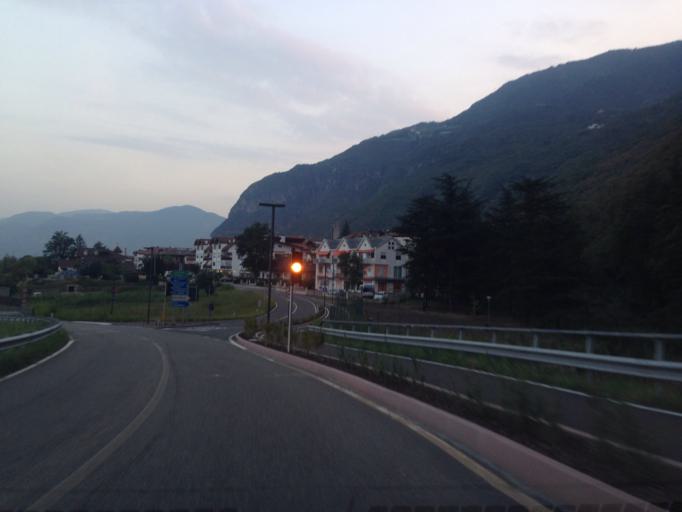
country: IT
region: Trentino-Alto Adige
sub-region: Bolzano
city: Pineta
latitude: 46.4344
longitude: 11.3469
